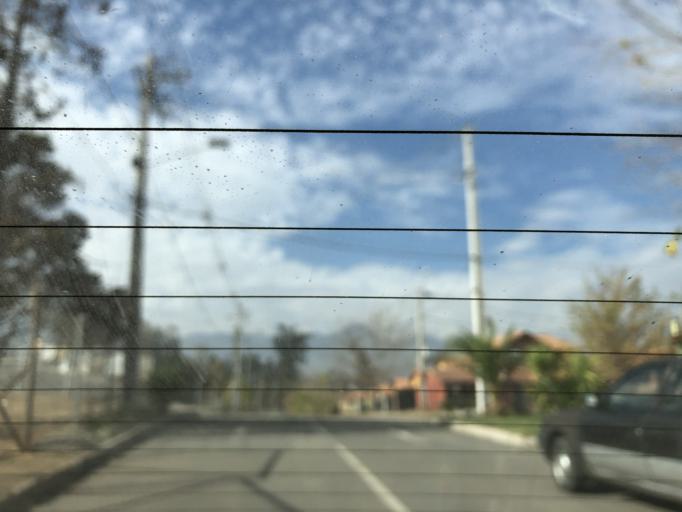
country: CL
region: Santiago Metropolitan
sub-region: Provincia de Cordillera
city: Puente Alto
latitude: -33.5887
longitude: -70.5373
